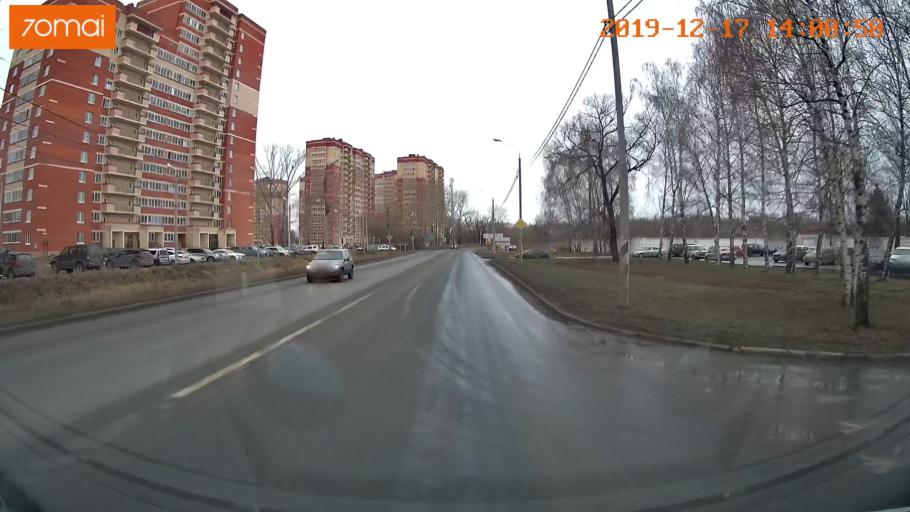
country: RU
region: Rjazan
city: Ryazan'
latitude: 54.6183
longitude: 39.6672
